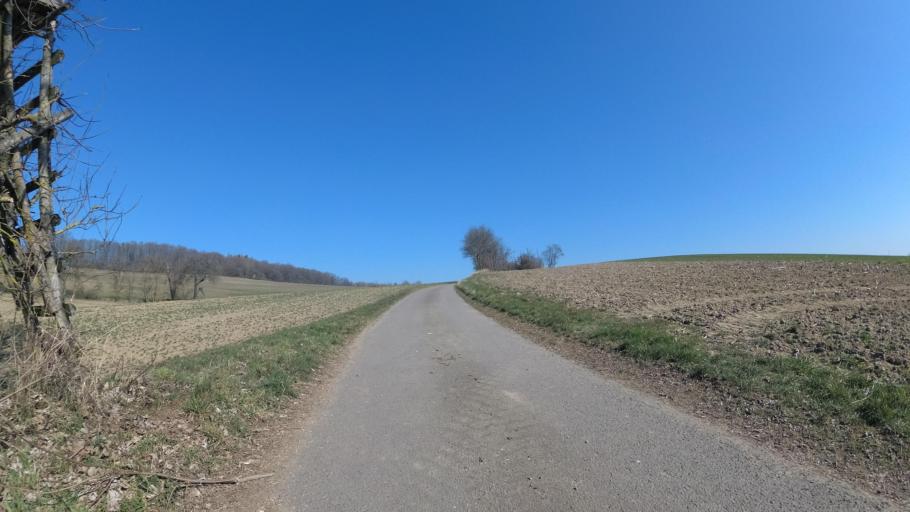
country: DE
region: Rheinland-Pfalz
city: Albessen
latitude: 49.5246
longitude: 7.3384
